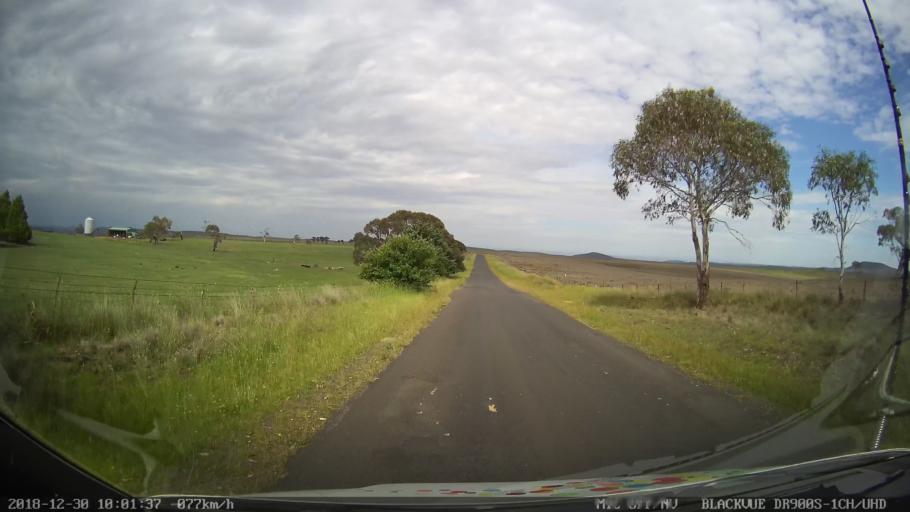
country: AU
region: New South Wales
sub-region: Cooma-Monaro
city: Cooma
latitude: -36.5154
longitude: 149.1832
